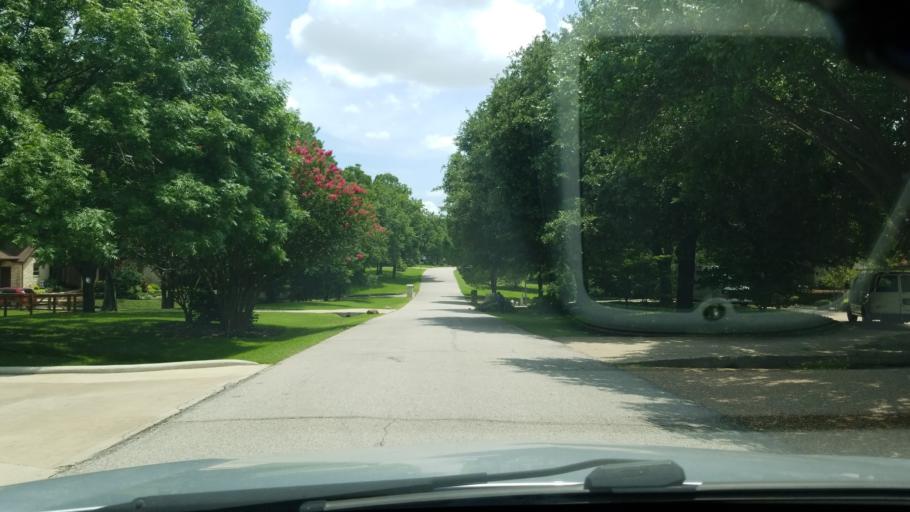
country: US
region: Texas
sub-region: Dallas County
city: Coppell
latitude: 32.9591
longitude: -96.9821
